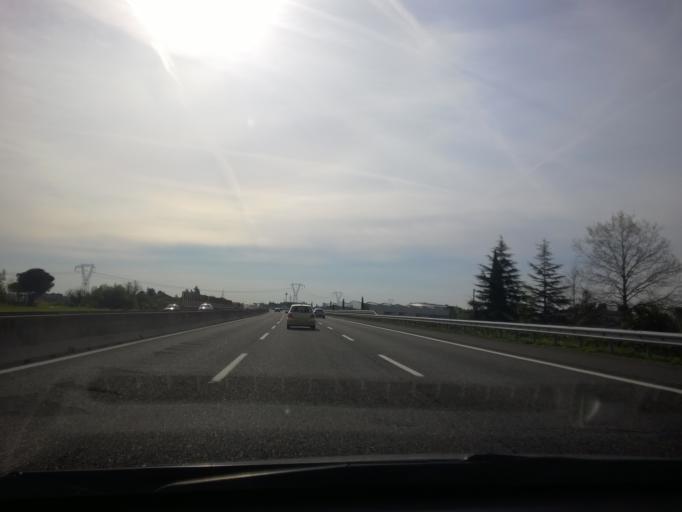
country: IT
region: Emilia-Romagna
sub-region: Forli-Cesena
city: Cesena
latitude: 44.1750
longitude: 12.2715
